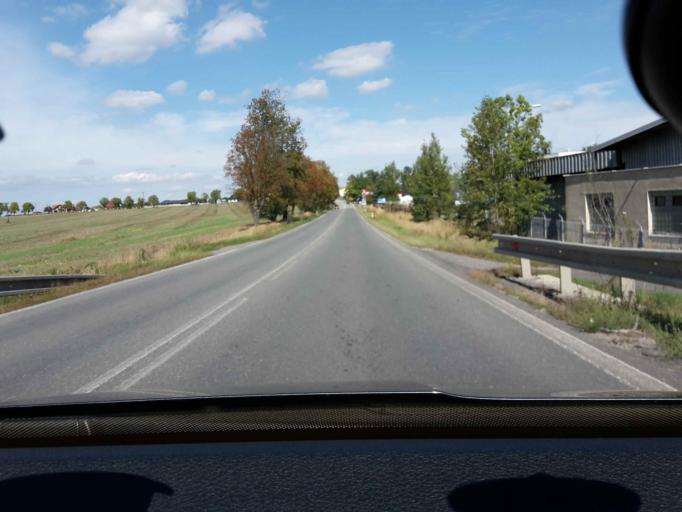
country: CZ
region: Jihocesky
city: Sobeslav
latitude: 49.2673
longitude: 14.7139
